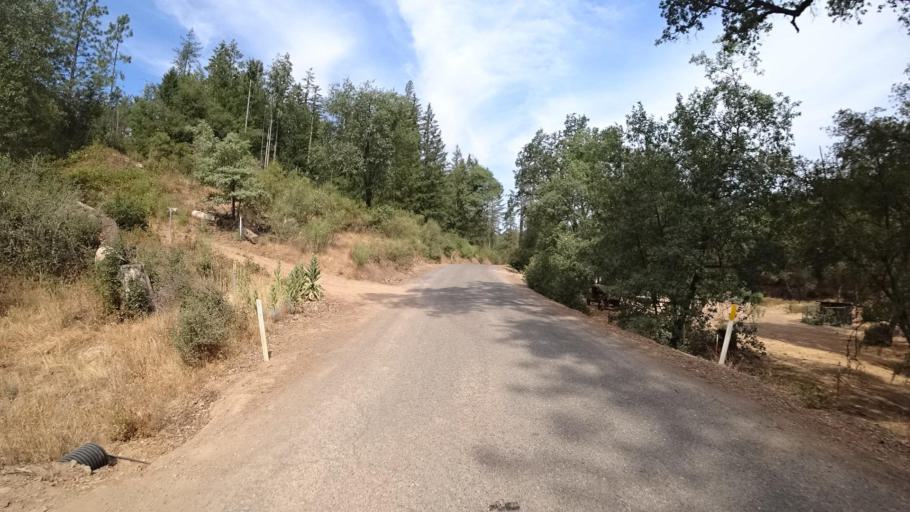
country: US
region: California
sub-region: Mariposa County
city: Midpines
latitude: 37.5640
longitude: -119.9784
